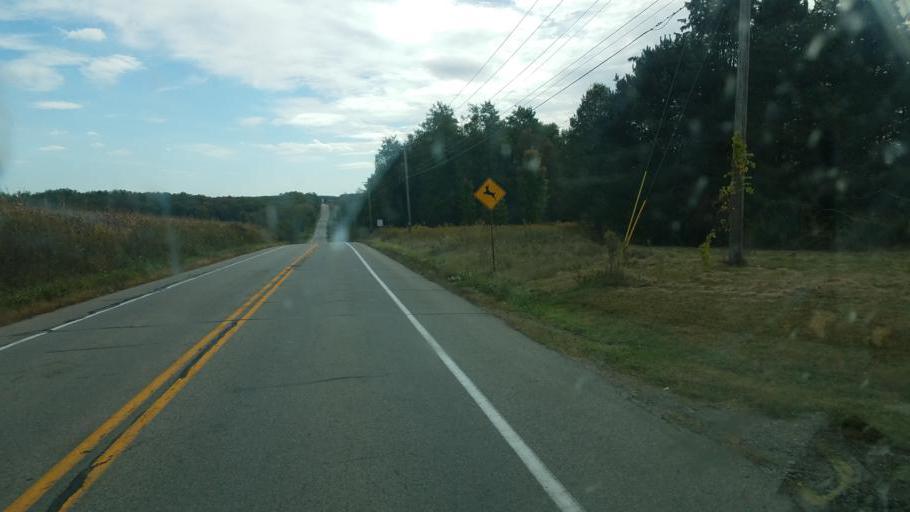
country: US
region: Pennsylvania
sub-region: Mercer County
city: Mercer
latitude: 41.2078
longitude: -80.2400
